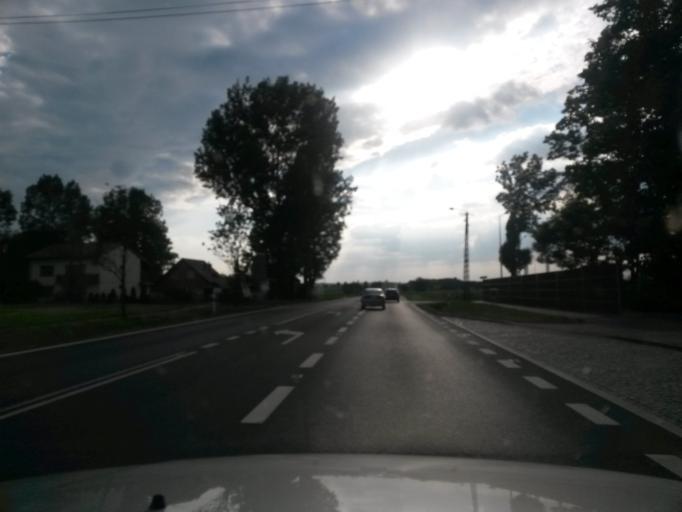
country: PL
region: Lodz Voivodeship
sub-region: Powiat piotrkowski
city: Grabica
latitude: 51.4160
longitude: 19.5609
